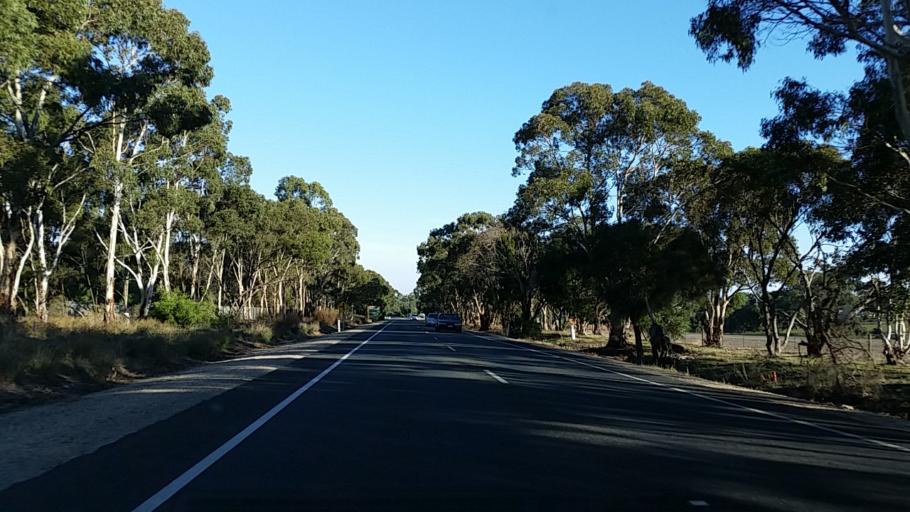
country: AU
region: South Australia
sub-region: Alexandrina
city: Strathalbyn
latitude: -35.2391
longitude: 138.8943
